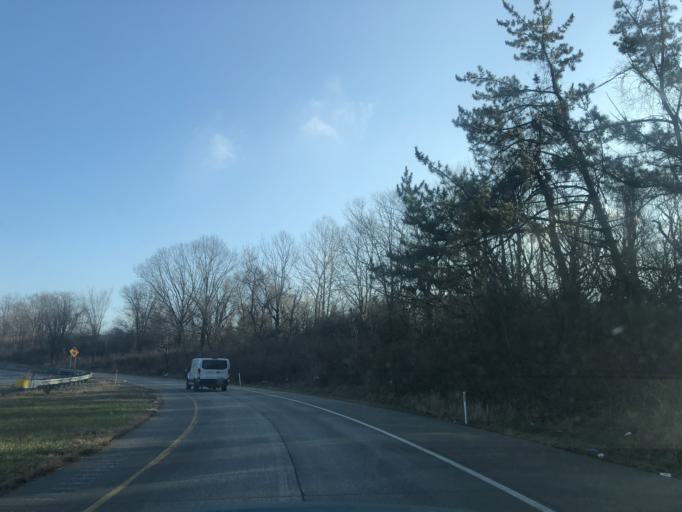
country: US
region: Pennsylvania
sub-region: Montgomery County
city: Conshohocken
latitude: 40.0953
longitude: -75.3020
